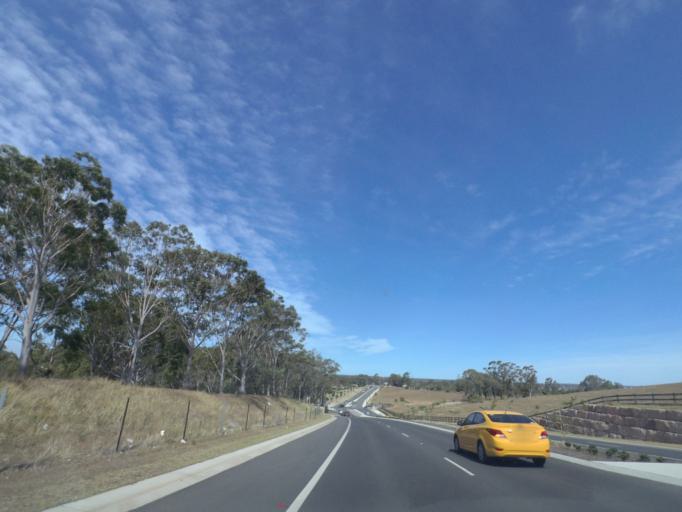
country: AU
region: New South Wales
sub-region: Campbelltown Municipality
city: Campbelltown
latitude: -34.0445
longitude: 150.7972
